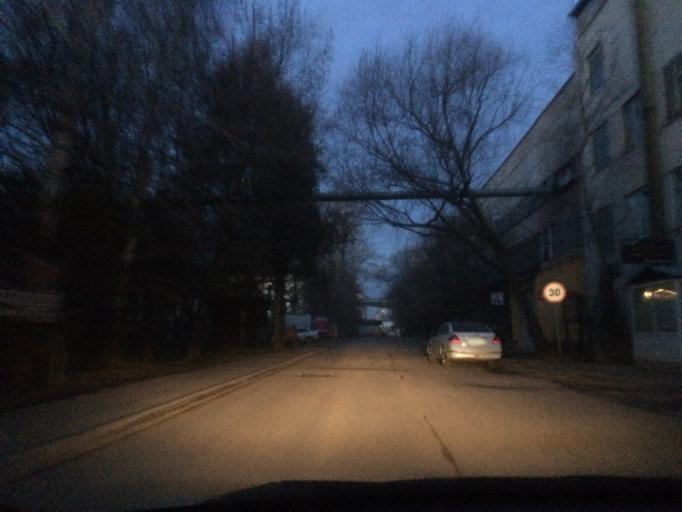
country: KZ
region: Astana Qalasy
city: Astana
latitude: 51.1849
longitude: 71.4247
